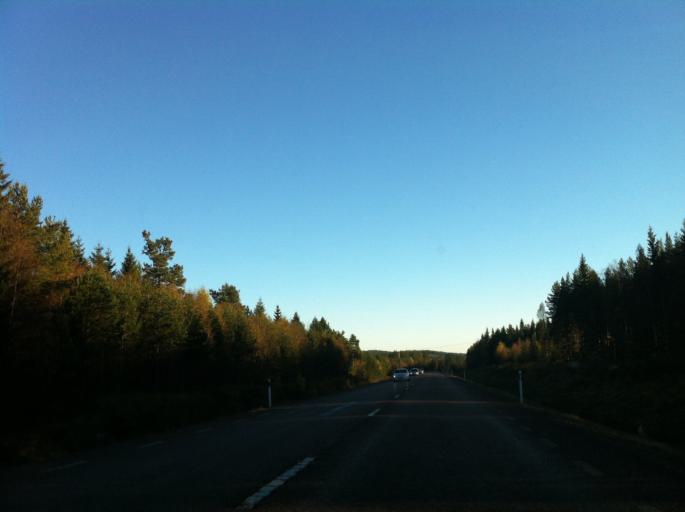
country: SE
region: Dalarna
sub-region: Rattviks Kommun
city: Raettvik
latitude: 60.8275
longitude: 15.2453
